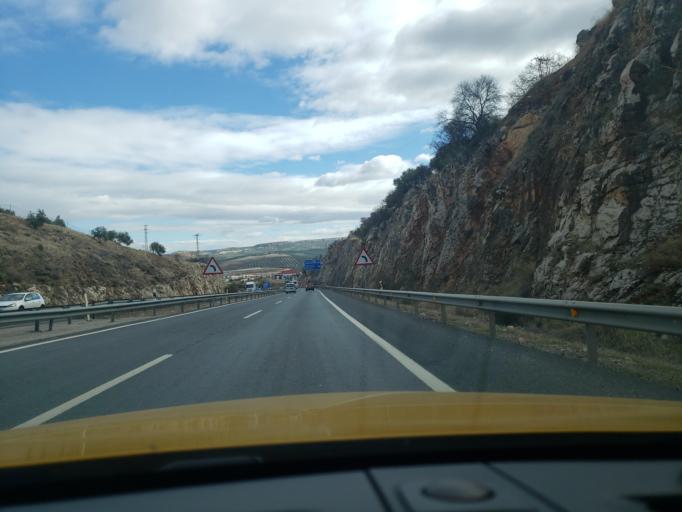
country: ES
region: Andalusia
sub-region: Provincia de Granada
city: Loja
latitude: 37.1602
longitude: -4.1369
